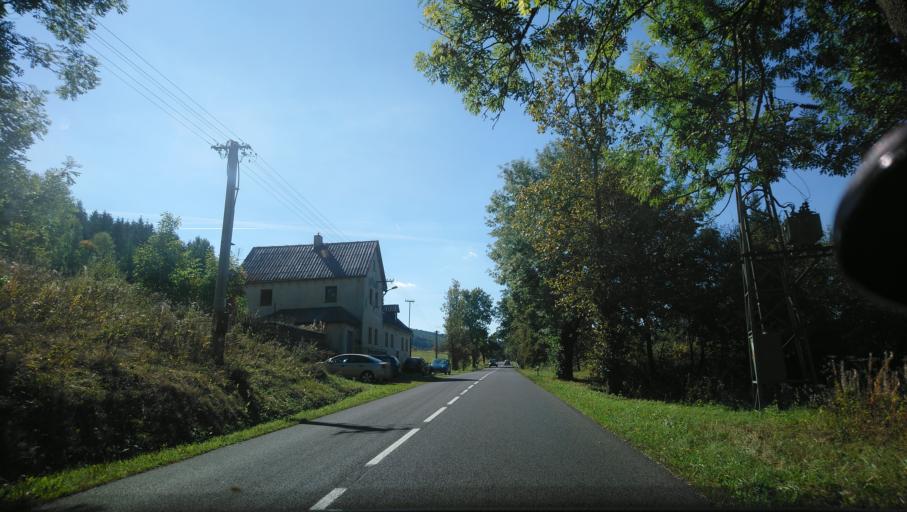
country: CZ
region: Ustecky
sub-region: Okres Chomutov
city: Kovarska
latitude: 50.4455
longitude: 13.0203
